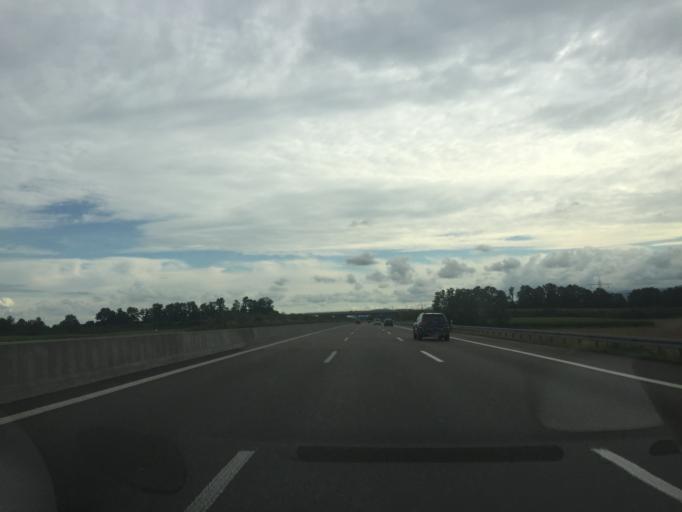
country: DE
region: Baden-Wuerttemberg
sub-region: Freiburg Region
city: Renchen
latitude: 48.6099
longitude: 7.9995
